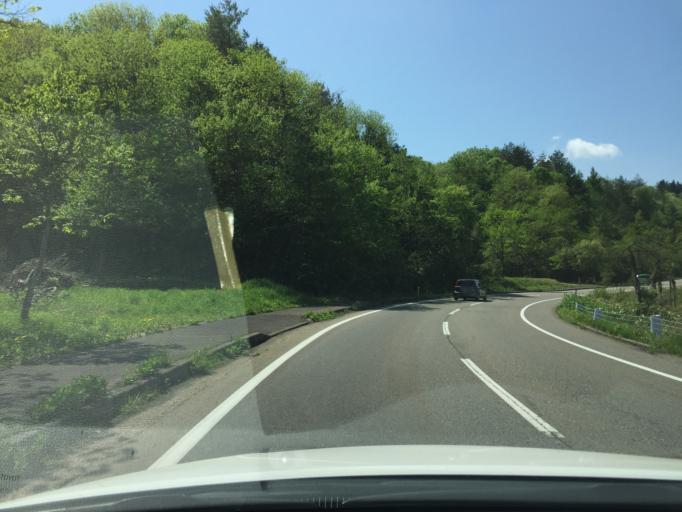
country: JP
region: Niigata
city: Kamo
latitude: 37.5985
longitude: 139.0951
